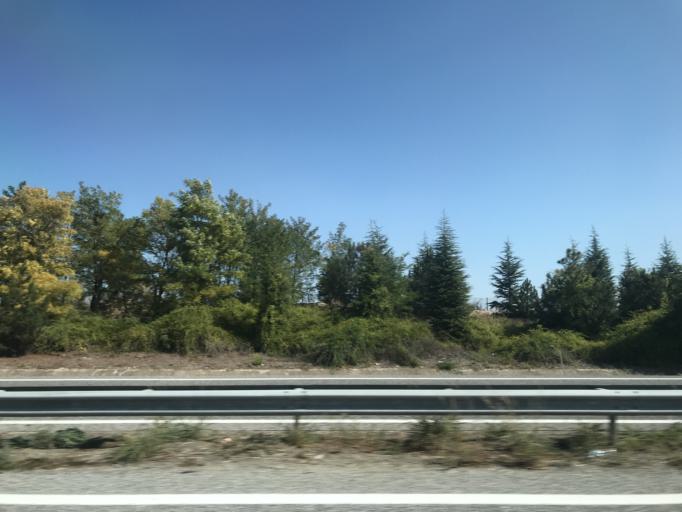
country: TR
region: Kirklareli
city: Luleburgaz
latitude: 41.4147
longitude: 27.3866
